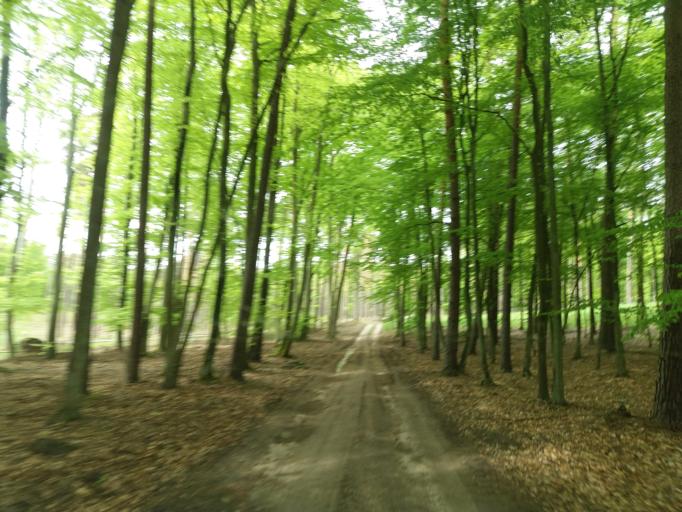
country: PL
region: West Pomeranian Voivodeship
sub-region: Powiat choszczenski
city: Bierzwnik
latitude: 53.0719
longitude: 15.6709
